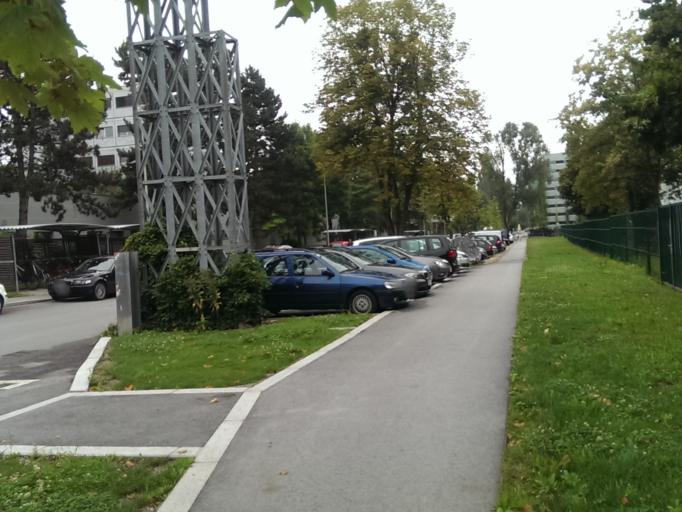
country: AT
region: Styria
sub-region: Graz Stadt
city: Graz
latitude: 47.0592
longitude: 15.4622
